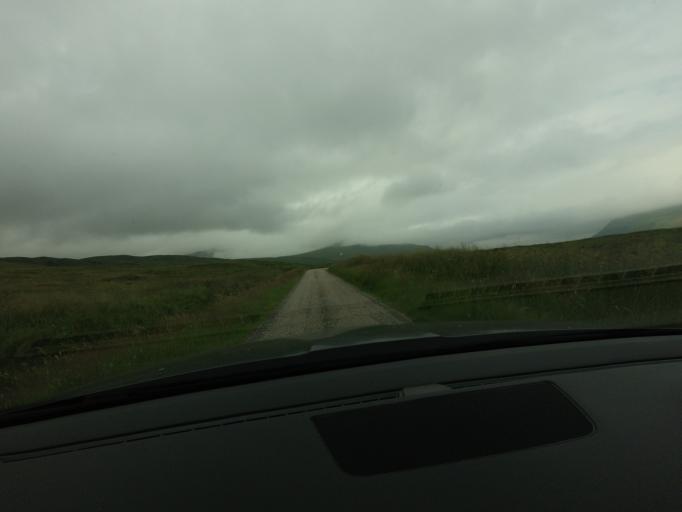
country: GB
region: Scotland
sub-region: Highland
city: Golspie
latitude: 58.3896
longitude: -4.3669
